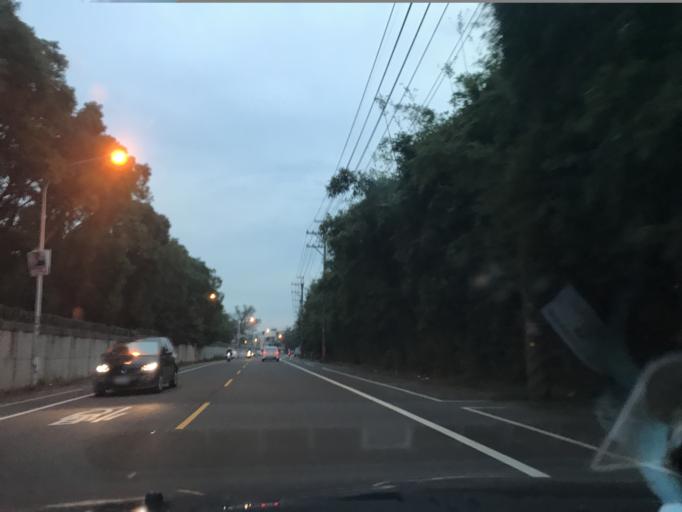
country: TW
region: Taiwan
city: Daxi
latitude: 24.9237
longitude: 121.2383
